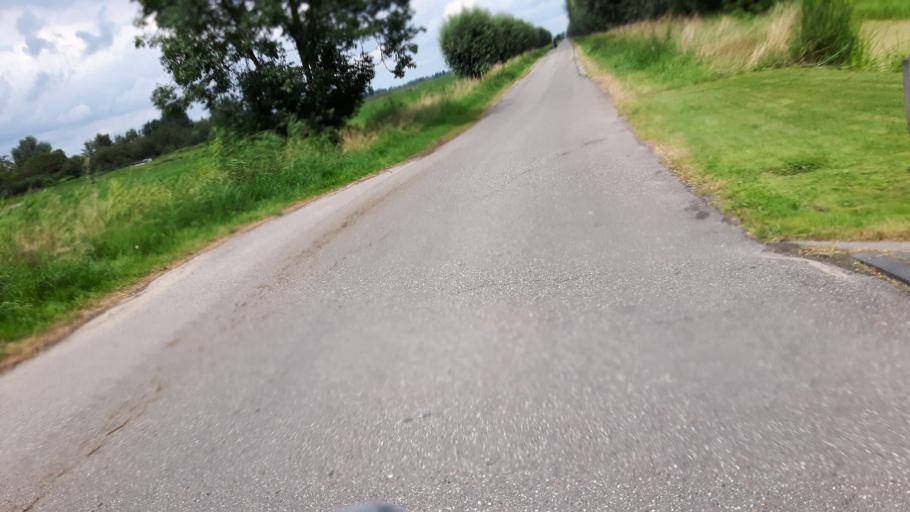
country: NL
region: South Holland
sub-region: Molenwaard
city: Nieuw-Lekkerland
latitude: 51.9012
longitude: 4.7253
